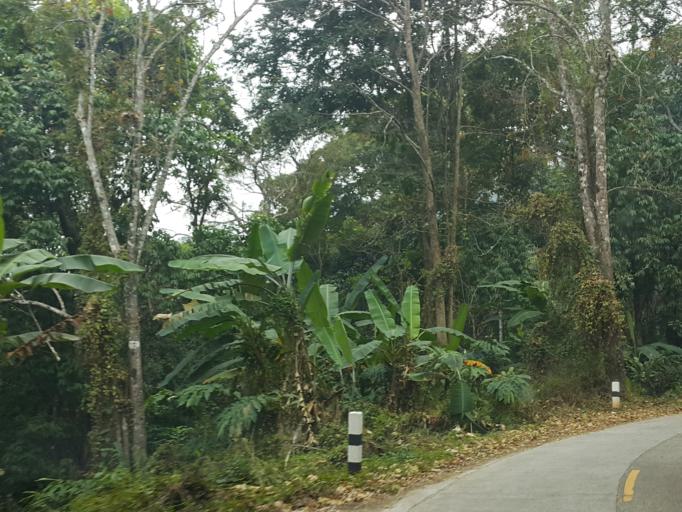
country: TH
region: Chiang Mai
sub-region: Amphoe Chiang Dao
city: Chiang Dao
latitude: 19.4113
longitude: 98.8822
